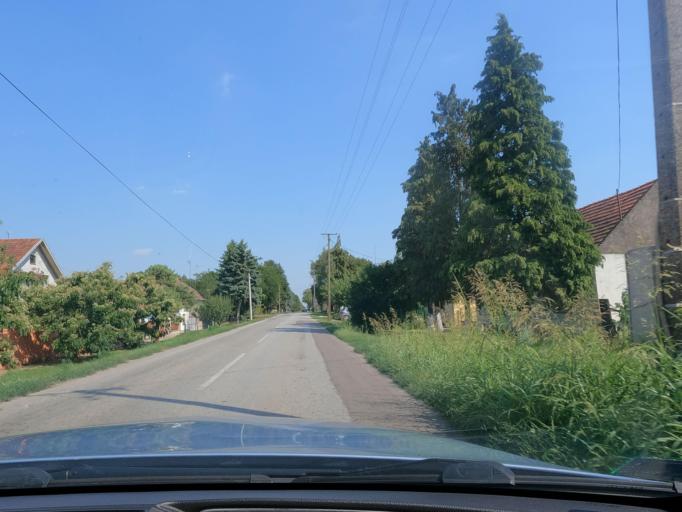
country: RS
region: Autonomna Pokrajina Vojvodina
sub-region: Severnobacki Okrug
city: Mali Igos
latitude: 45.7634
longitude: 19.7484
